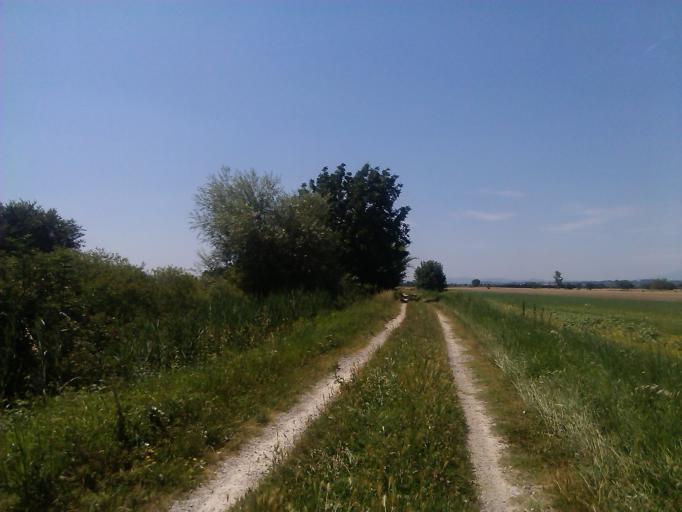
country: IT
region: Tuscany
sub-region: Province of Arezzo
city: Cesa
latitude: 43.3453
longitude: 11.8264
